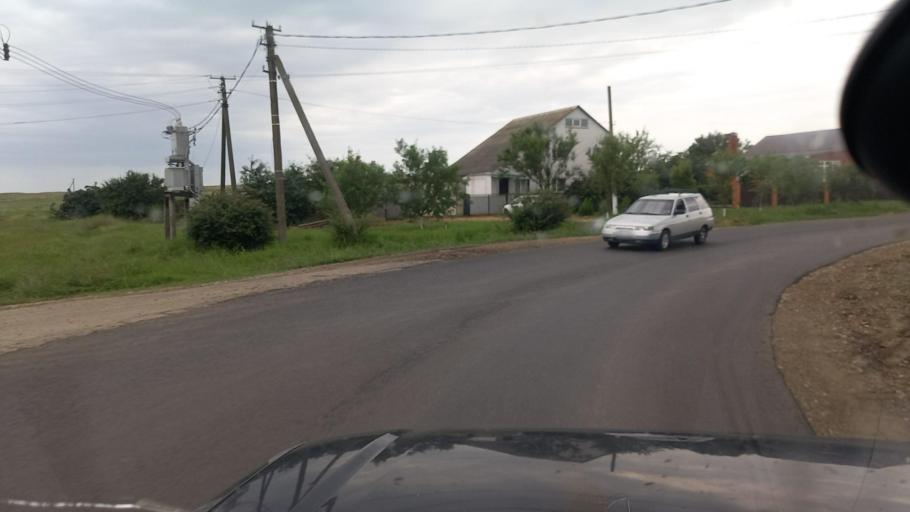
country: RU
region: Krasnodarskiy
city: Akhtanizovskaya
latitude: 45.3339
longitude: 37.1213
